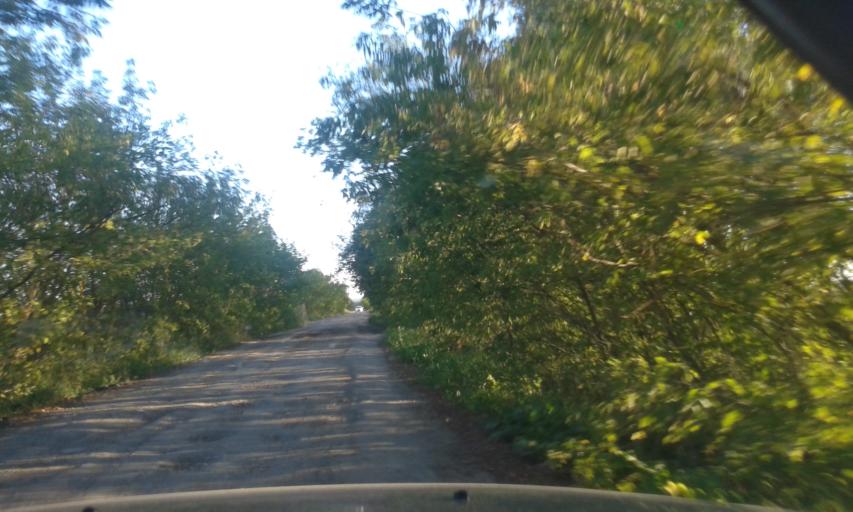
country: RU
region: Tula
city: Krapivna
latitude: 54.1306
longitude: 37.1570
